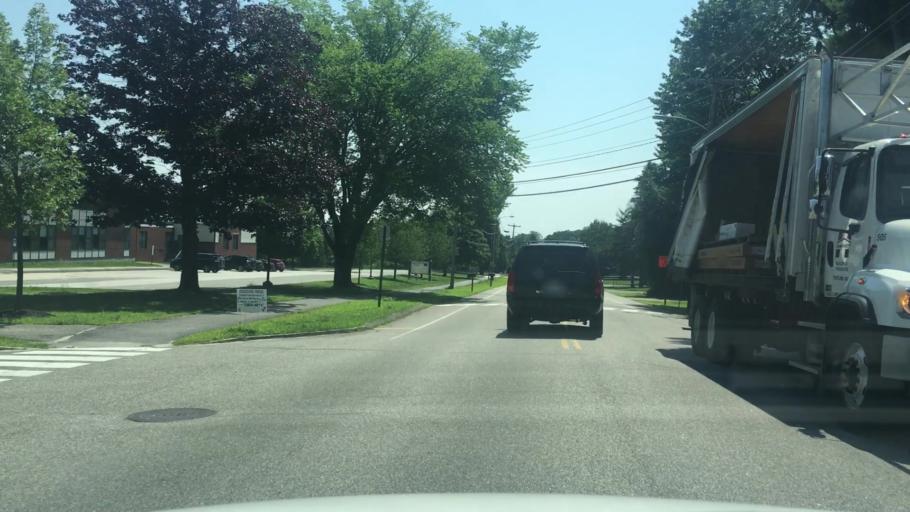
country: US
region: Maine
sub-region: Cumberland County
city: Cumberland Center
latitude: 43.7951
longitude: -70.2558
